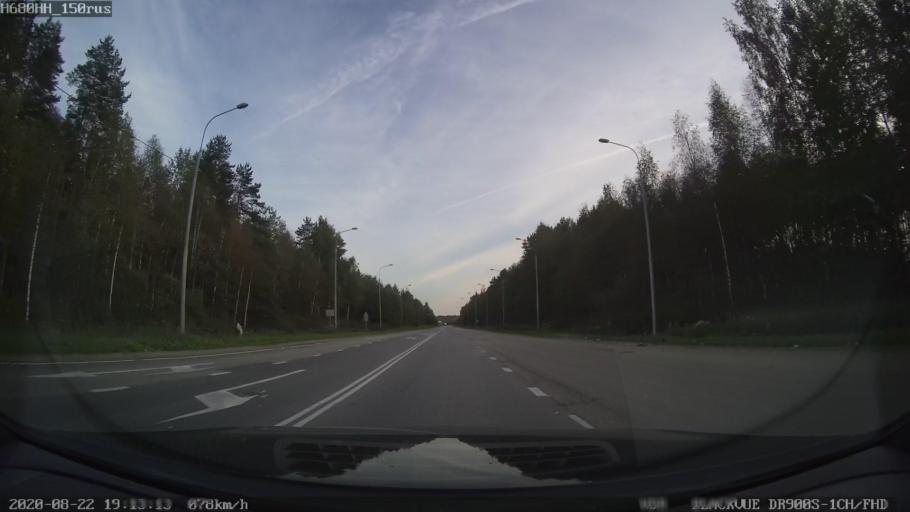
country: RU
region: Tverskaya
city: Sakharovo
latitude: 56.9949
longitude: 36.0259
